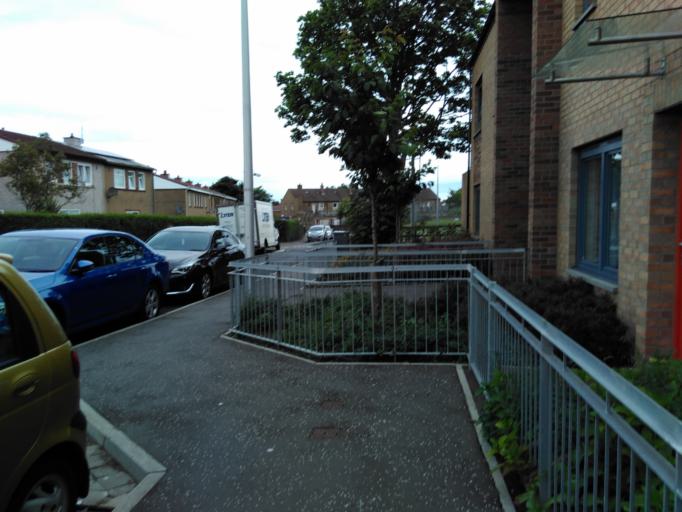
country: GB
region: Scotland
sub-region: Midlothian
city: Loanhead
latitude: 55.9124
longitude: -3.1368
